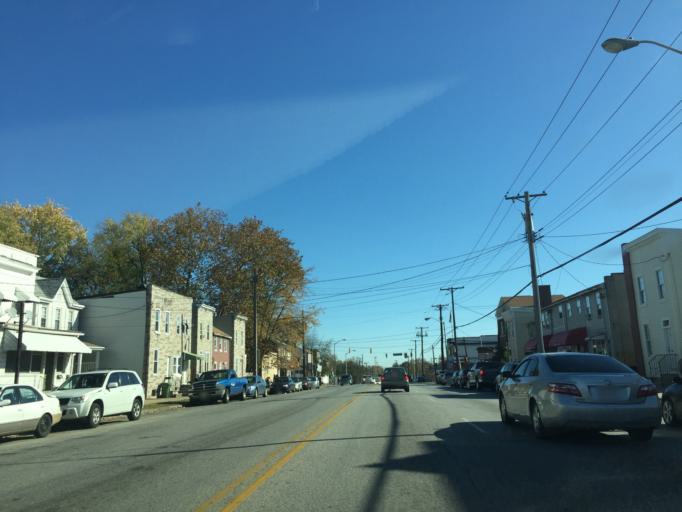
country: US
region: Maryland
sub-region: Anne Arundel County
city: Brooklyn Park
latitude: 39.2367
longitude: -76.6036
